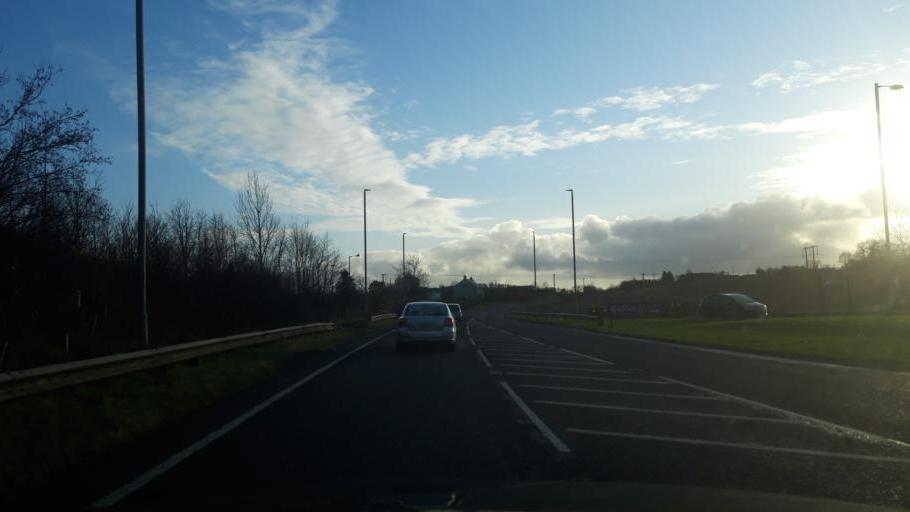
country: GB
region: Northern Ireland
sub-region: Dungannon District
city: Dungannon
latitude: 54.5432
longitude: -6.7781
